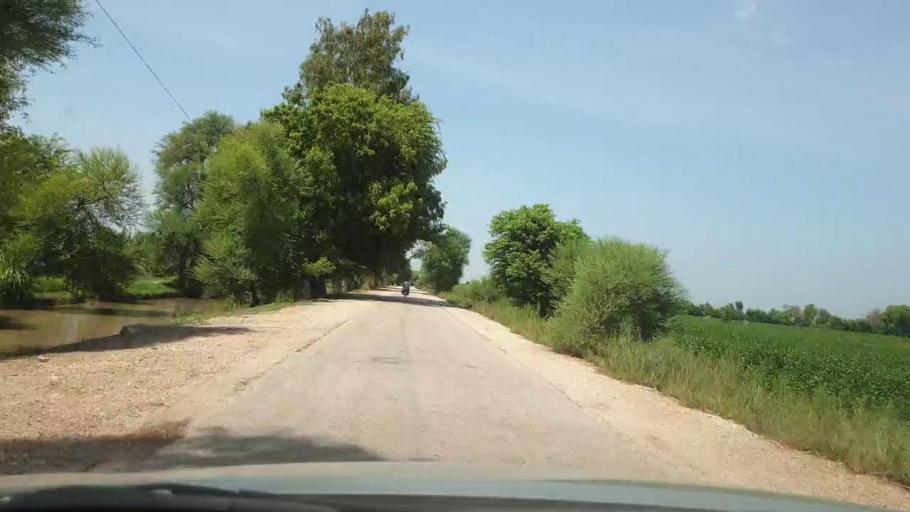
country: PK
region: Sindh
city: Pano Aqil
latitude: 27.7033
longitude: 69.1126
